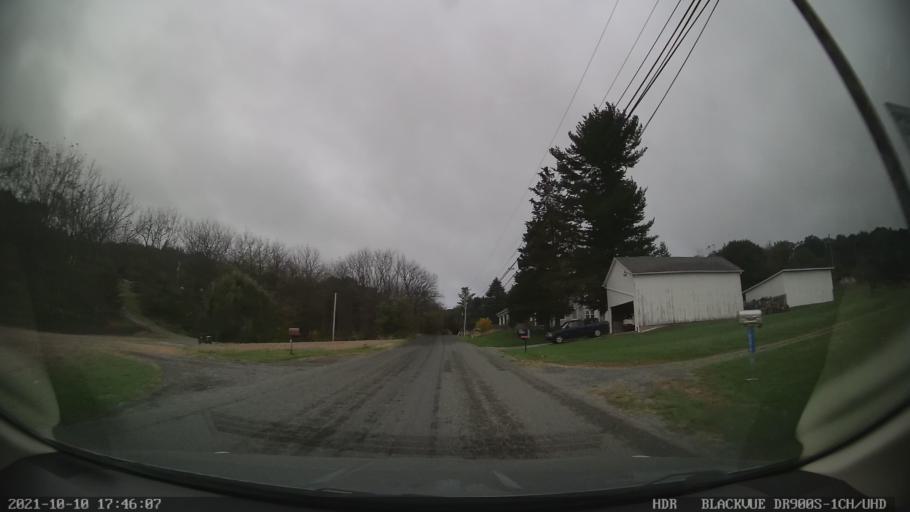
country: US
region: Pennsylvania
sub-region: Lehigh County
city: Breinigsville
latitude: 40.5593
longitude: -75.6750
